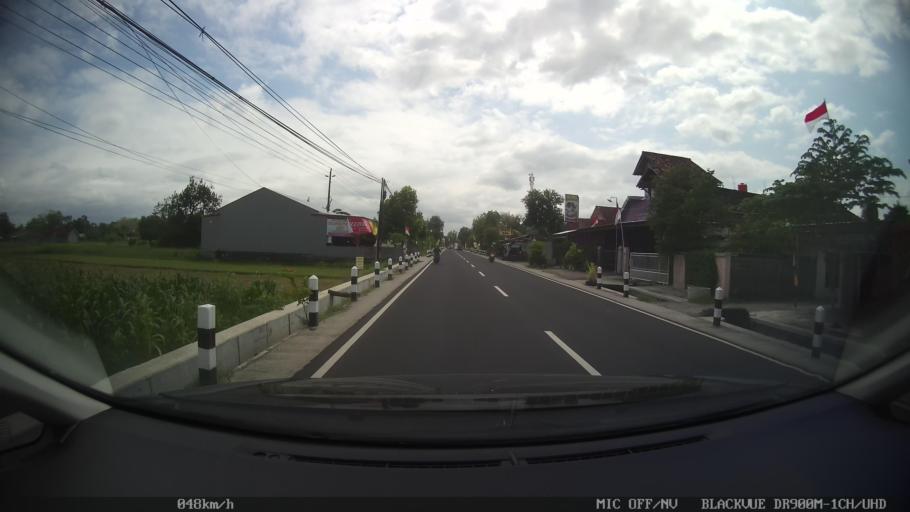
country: ID
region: Central Java
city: Candi Prambanan
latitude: -7.8139
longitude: 110.4822
